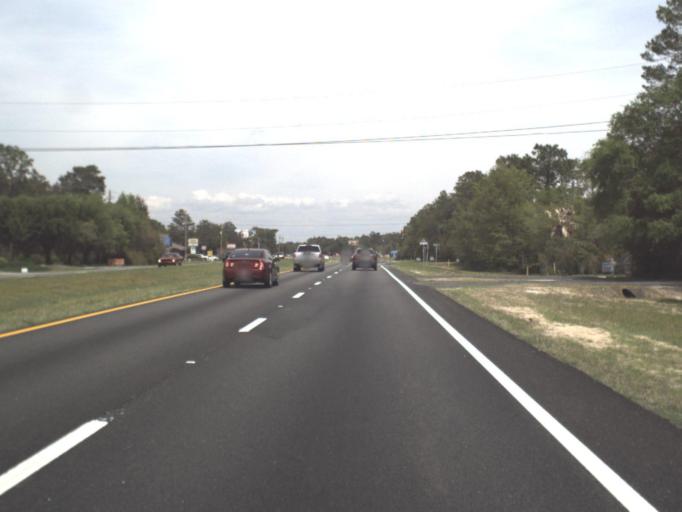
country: US
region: Florida
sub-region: Okaloosa County
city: Ocean City
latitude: 30.4679
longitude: -86.6118
